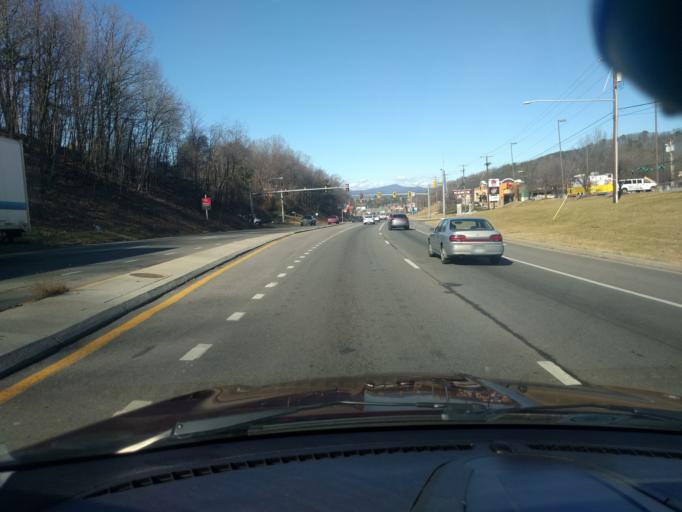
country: US
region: Virginia
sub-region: Roanoke County
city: Narrows
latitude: 37.2214
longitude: -79.9675
